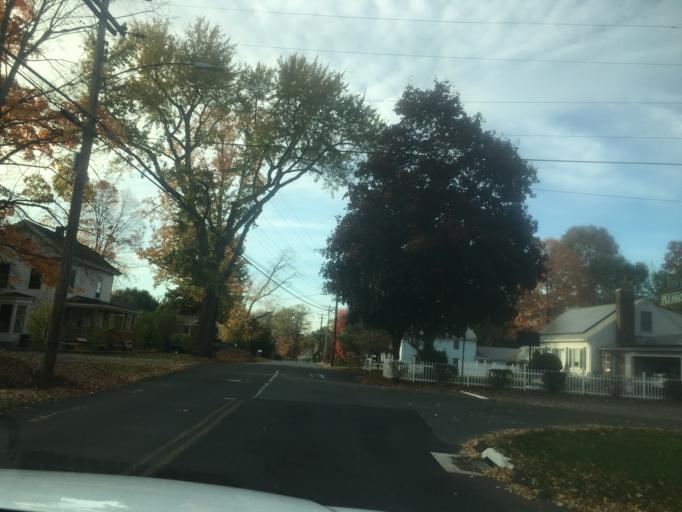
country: US
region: Connecticut
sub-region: Hartford County
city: South Windsor
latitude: 41.8140
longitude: -72.5938
